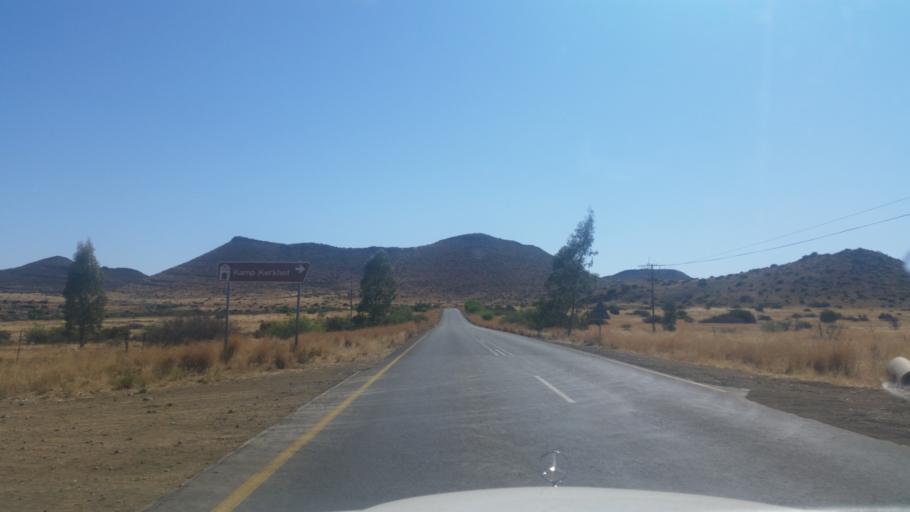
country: ZA
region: Orange Free State
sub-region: Xhariep District Municipality
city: Trompsburg
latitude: -30.4853
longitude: 25.9962
